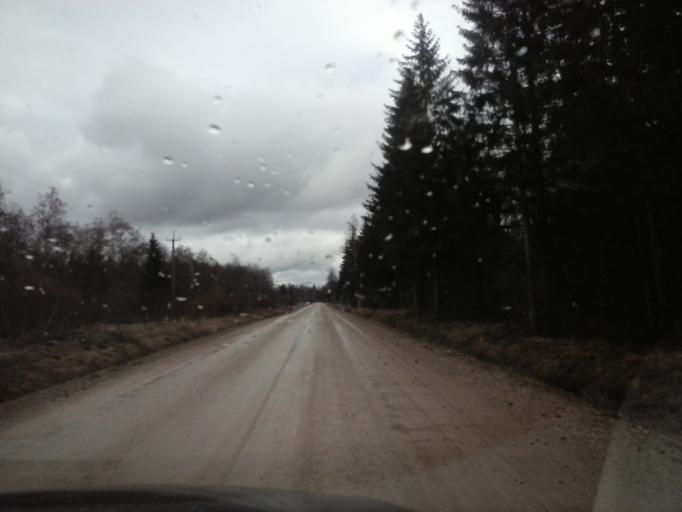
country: EE
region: Ida-Virumaa
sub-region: Kivioli linn
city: Kivioli
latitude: 59.1084
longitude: 26.9205
